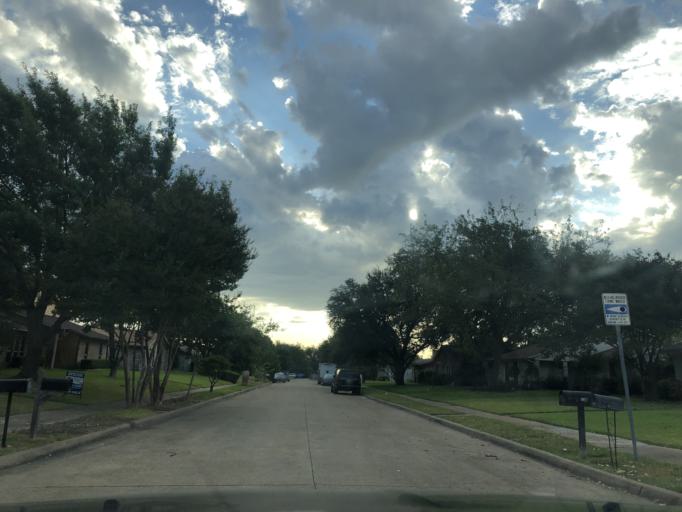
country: US
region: Texas
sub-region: Dallas County
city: Garland
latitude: 32.8736
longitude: -96.6564
